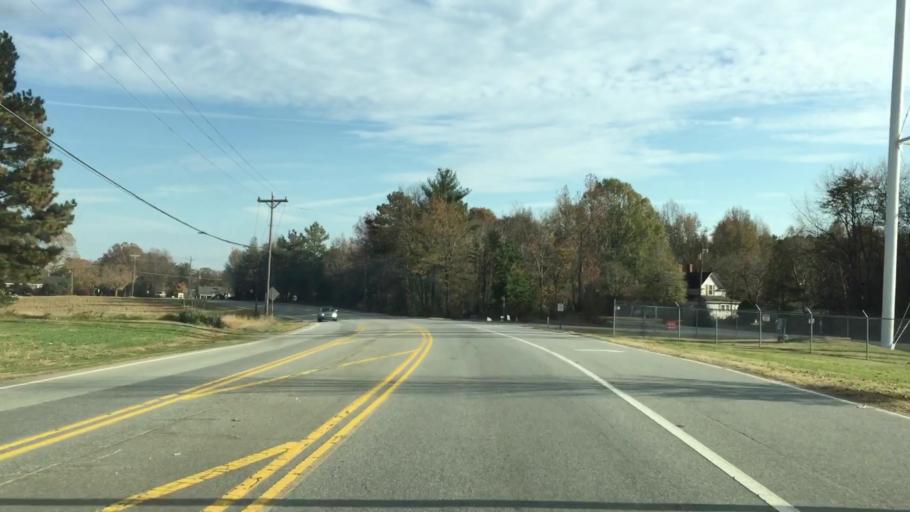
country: US
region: North Carolina
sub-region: Guilford County
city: Stokesdale
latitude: 36.2358
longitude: -79.9776
